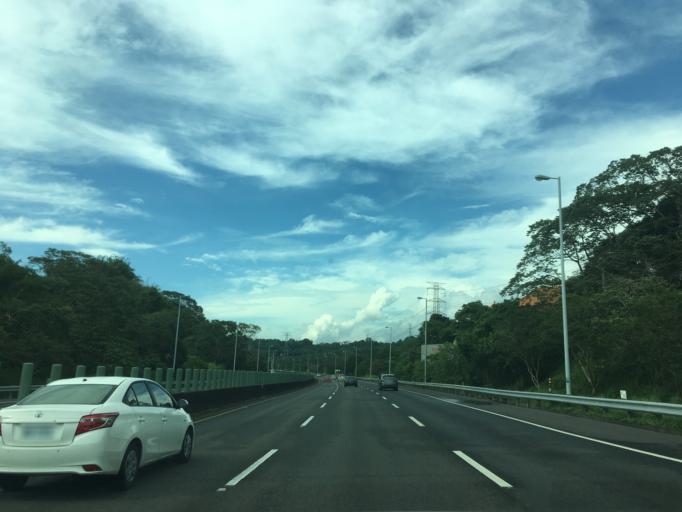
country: TW
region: Taiwan
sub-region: Chiayi
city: Jiayi Shi
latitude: 23.4643
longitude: 120.4969
